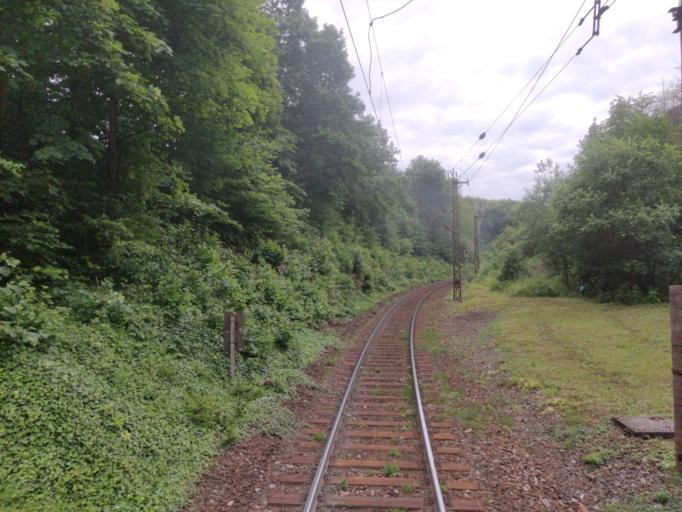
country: DE
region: Saxony-Anhalt
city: Huttenrode
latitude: 51.7733
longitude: 10.9043
